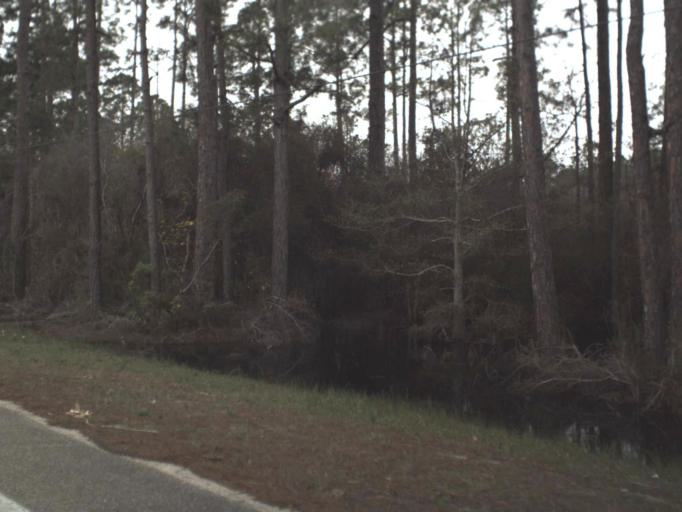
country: US
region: Florida
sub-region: Gulf County
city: Port Saint Joe
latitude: 29.8252
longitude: -85.2805
